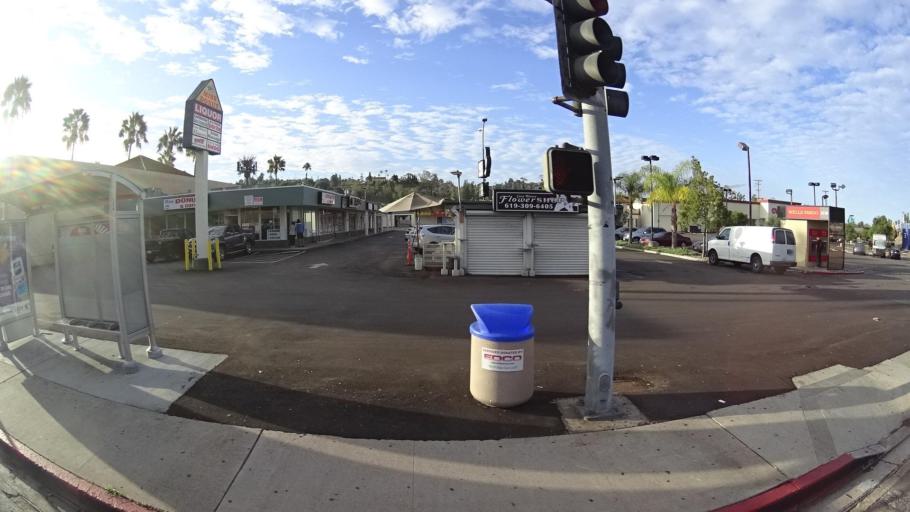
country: US
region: California
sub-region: San Diego County
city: Spring Valley
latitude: 32.7479
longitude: -116.9872
